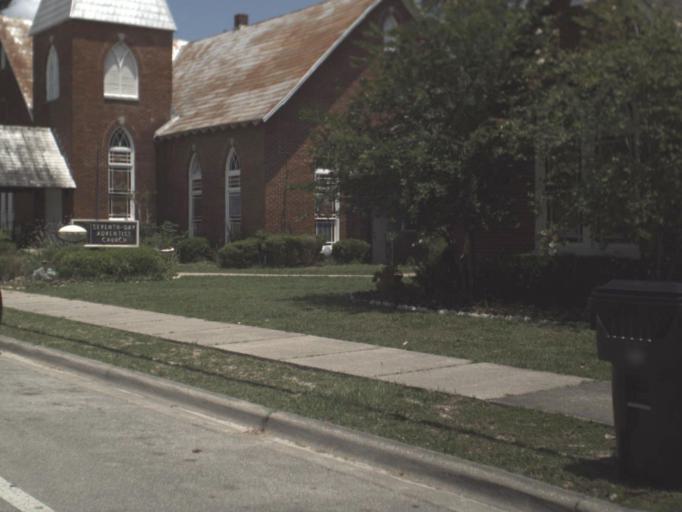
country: US
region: Florida
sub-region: Alachua County
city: High Springs
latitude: 29.8281
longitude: -82.5994
